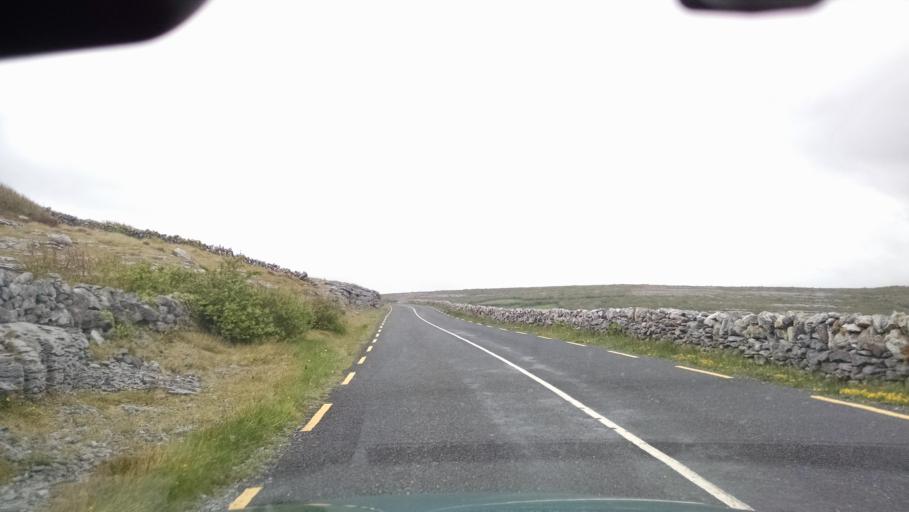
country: IE
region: Connaught
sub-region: County Galway
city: Bearna
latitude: 53.0824
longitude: -9.1654
